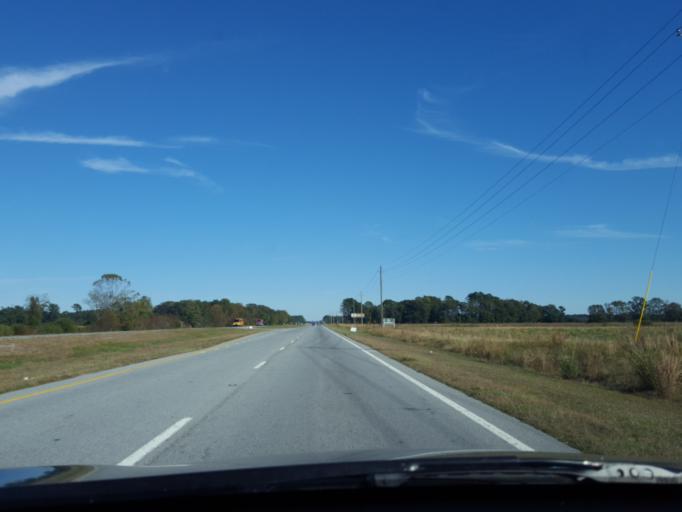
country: US
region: North Carolina
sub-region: Pitt County
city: Greenville
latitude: 35.6257
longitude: -77.3084
